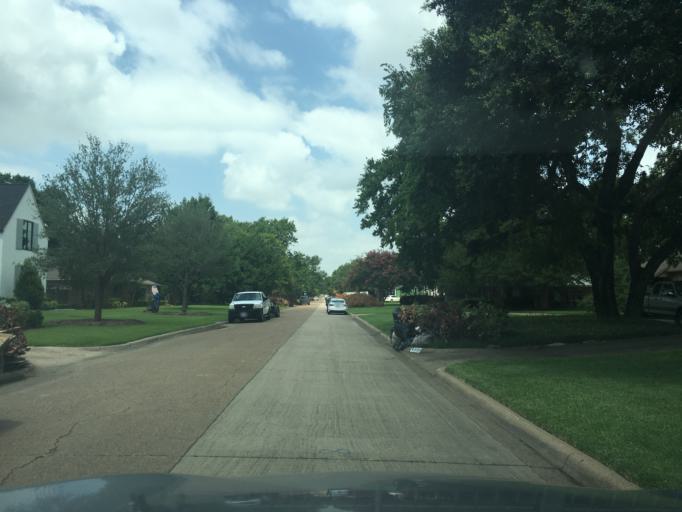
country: US
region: Texas
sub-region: Dallas County
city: Addison
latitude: 32.9169
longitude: -96.8215
